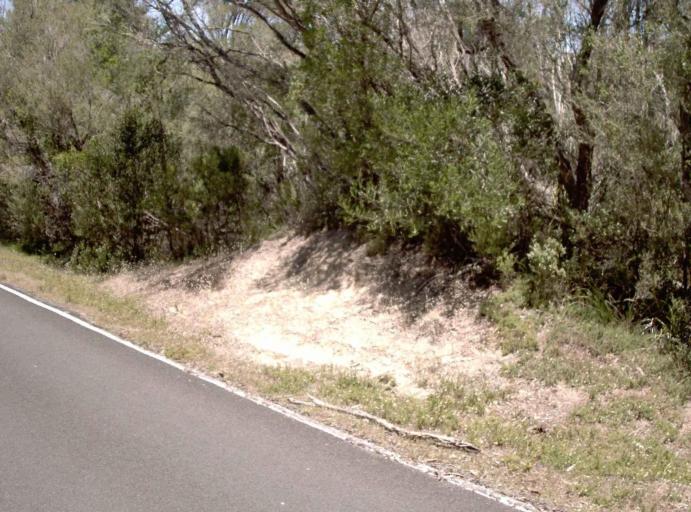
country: AU
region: Victoria
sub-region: Latrobe
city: Morwell
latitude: -38.8694
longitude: 146.2640
